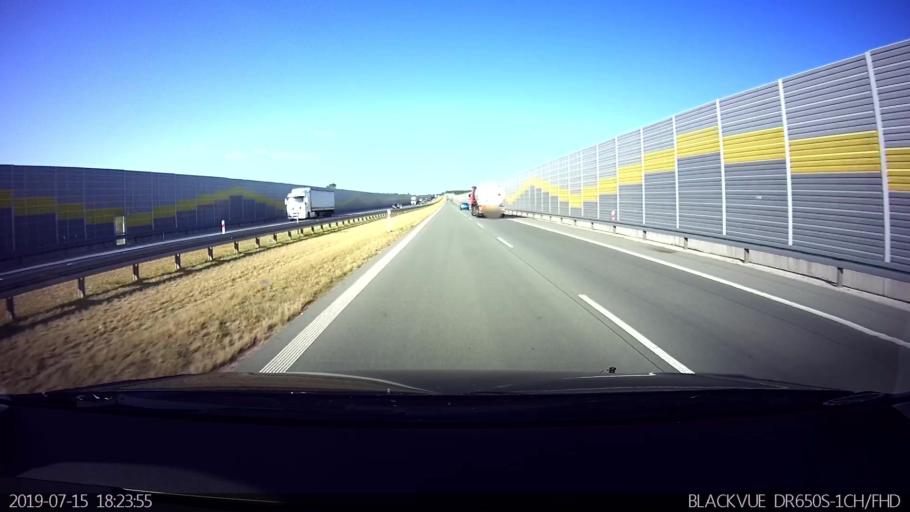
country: PL
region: Lodz Voivodeship
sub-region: Powiat laski
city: Lask
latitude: 51.5636
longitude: 19.1442
